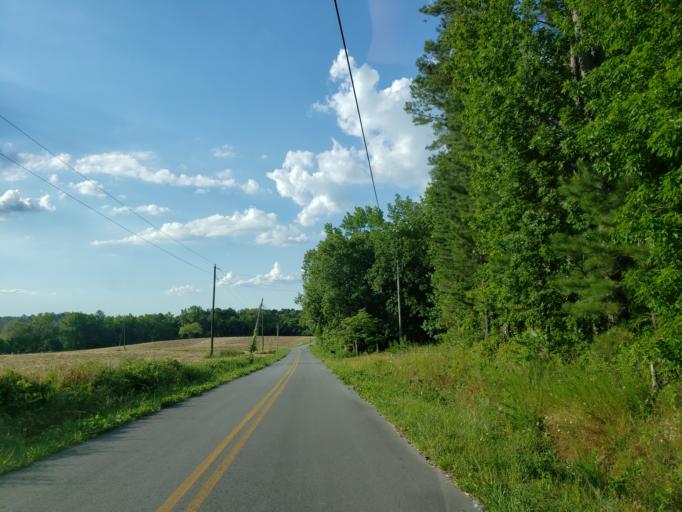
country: US
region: Georgia
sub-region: Haralson County
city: Buchanan
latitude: 33.9056
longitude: -85.2743
